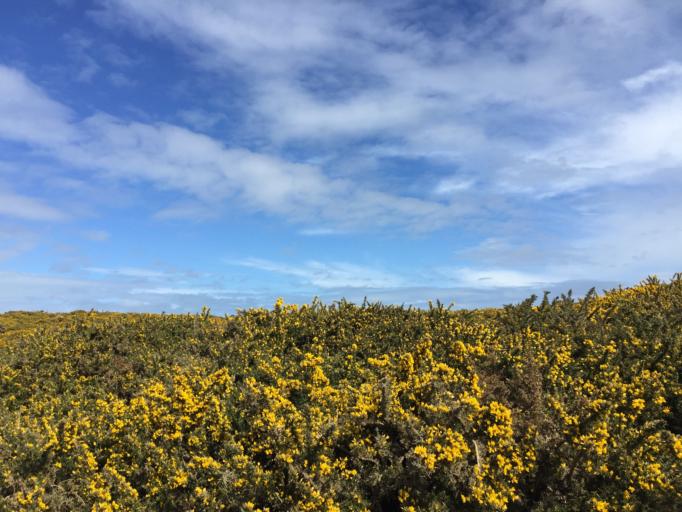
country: JE
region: St Helier
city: Saint Helier
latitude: 49.1706
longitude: -2.1728
